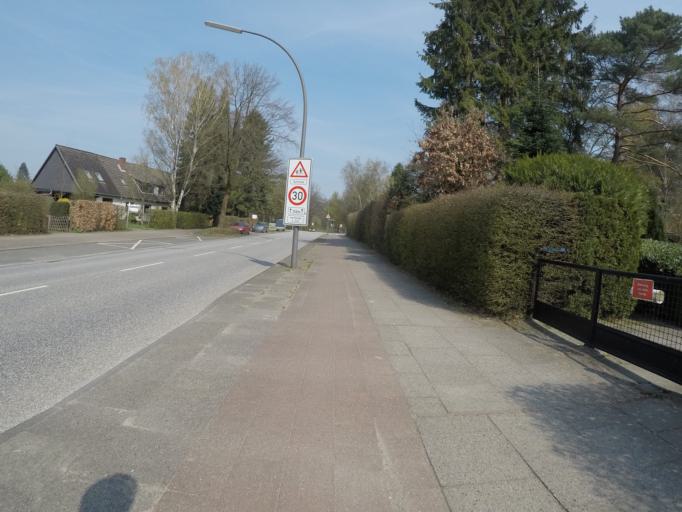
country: DE
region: Hamburg
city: Hummelsbuettel
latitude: 53.6436
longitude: 10.0506
